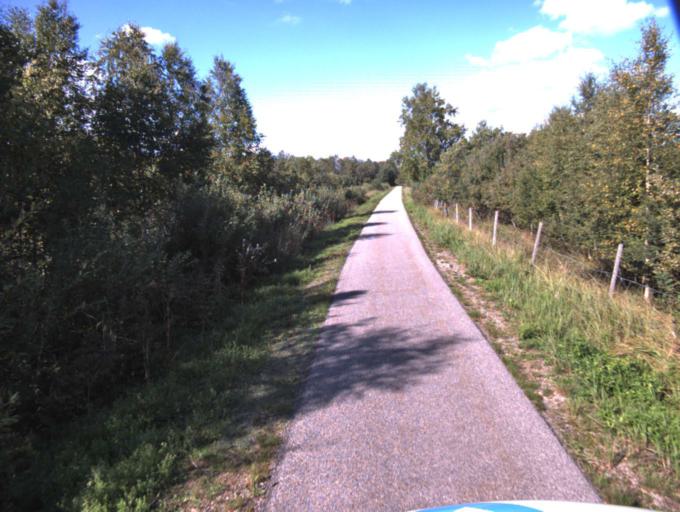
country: SE
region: Vaestra Goetaland
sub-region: Ulricehamns Kommun
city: Ulricehamn
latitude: 57.8406
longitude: 13.3038
